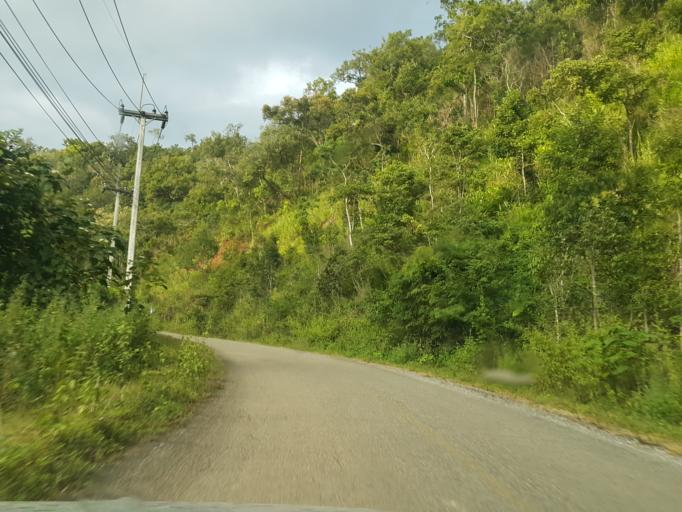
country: TH
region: Mae Hong Son
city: Khun Yuam
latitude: 18.7504
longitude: 98.1943
